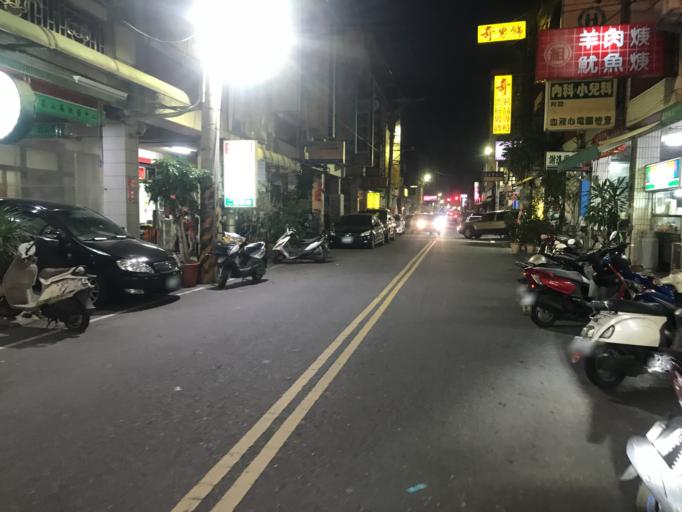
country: TW
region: Taiwan
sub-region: Nantou
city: Nantou
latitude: 23.8618
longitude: 120.5859
